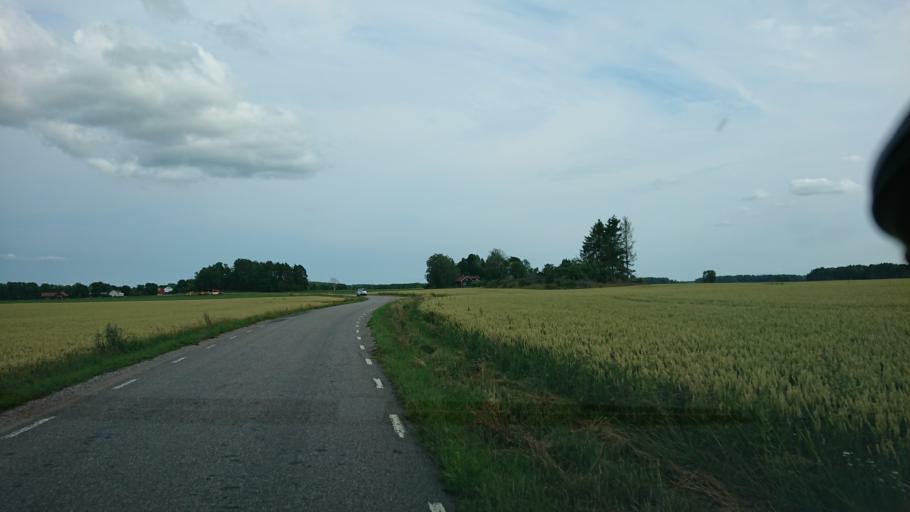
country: SE
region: Uppsala
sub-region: Osthammars Kommun
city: Bjorklinge
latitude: 59.9883
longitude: 17.5450
